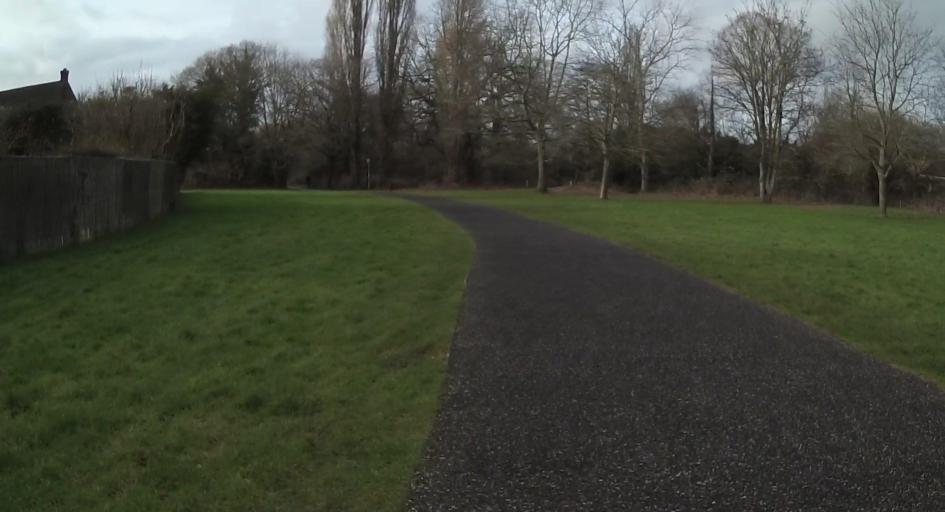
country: GB
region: England
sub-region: Wokingham
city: Wokingham
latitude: 51.4102
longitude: -0.8493
